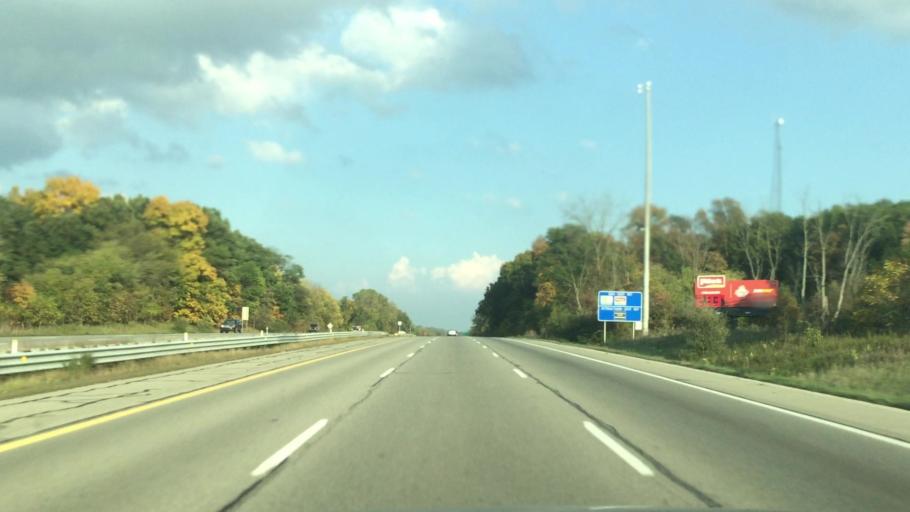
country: US
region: Michigan
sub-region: Washtenaw County
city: Dexter
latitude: 42.2978
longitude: -83.8917
